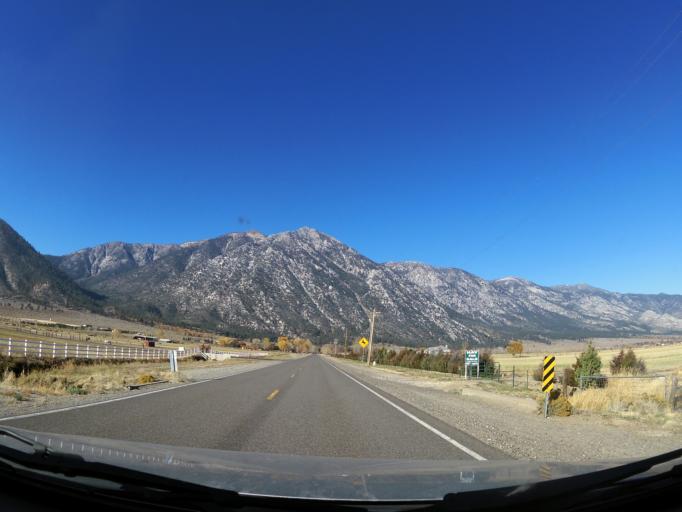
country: US
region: Nevada
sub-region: Douglas County
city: Gardnerville Ranchos
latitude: 38.8670
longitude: -119.7834
